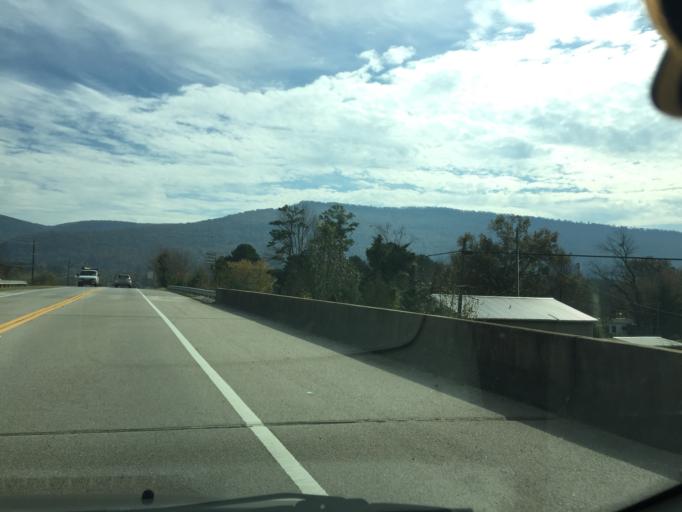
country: US
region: Georgia
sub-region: Dade County
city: Trenton
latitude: 34.8656
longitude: -85.5097
